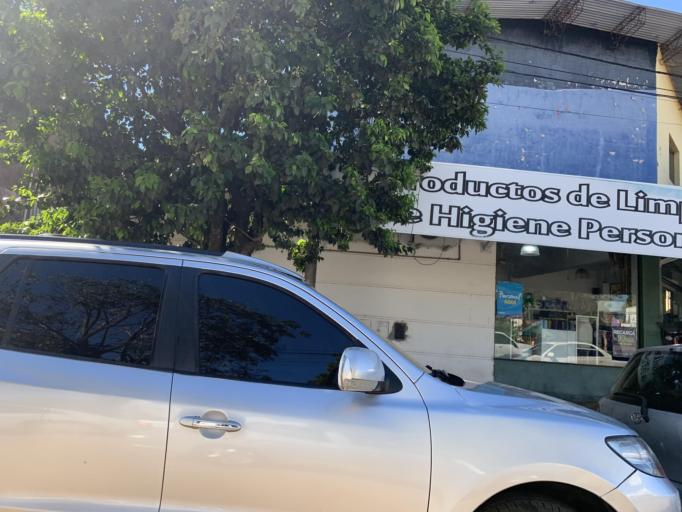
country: PY
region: Misiones
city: San Juan Bautista
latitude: -26.6696
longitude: -57.1420
